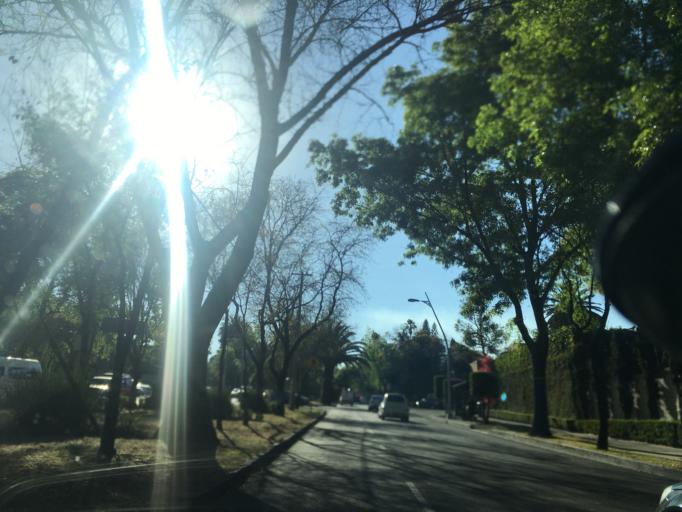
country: MX
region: Mexico City
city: Polanco
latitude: 19.4246
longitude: -99.2101
